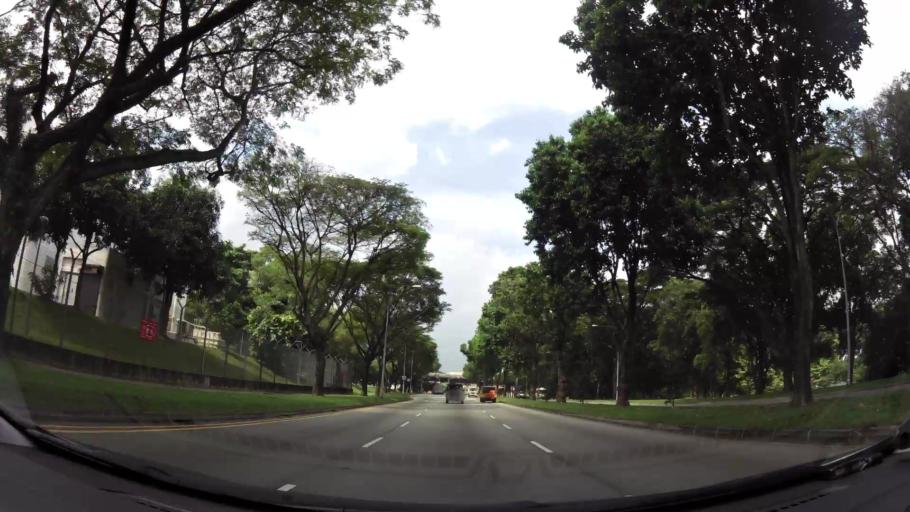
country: SG
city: Singapore
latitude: 1.3432
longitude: 103.9186
